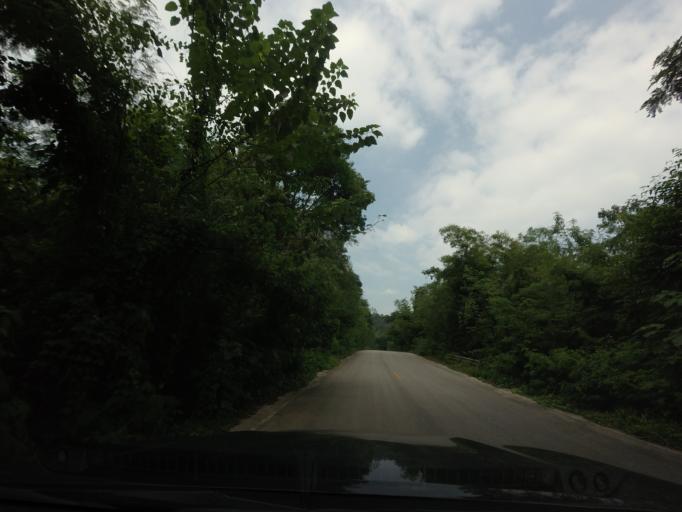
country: LA
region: Xiagnabouli
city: Muang Kenthao
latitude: 17.7437
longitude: 101.4790
